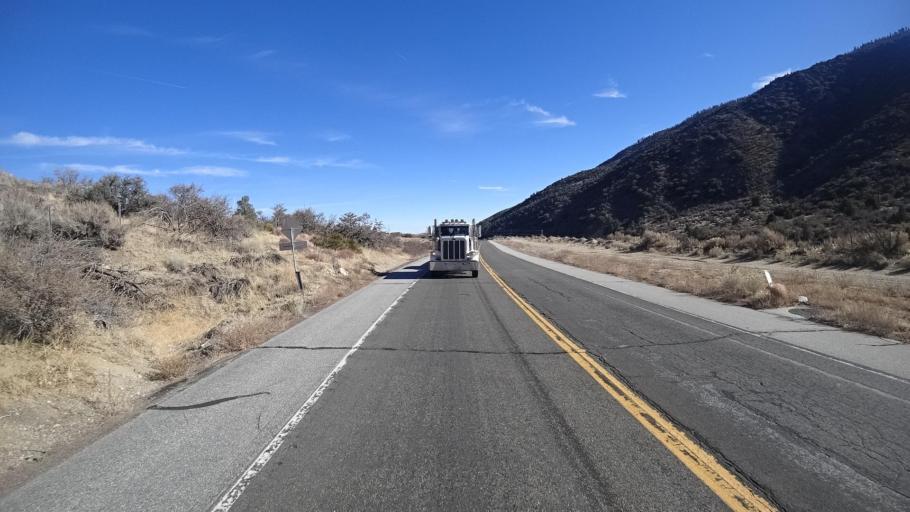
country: US
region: California
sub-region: Kern County
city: Frazier Park
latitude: 34.8210
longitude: -118.9670
